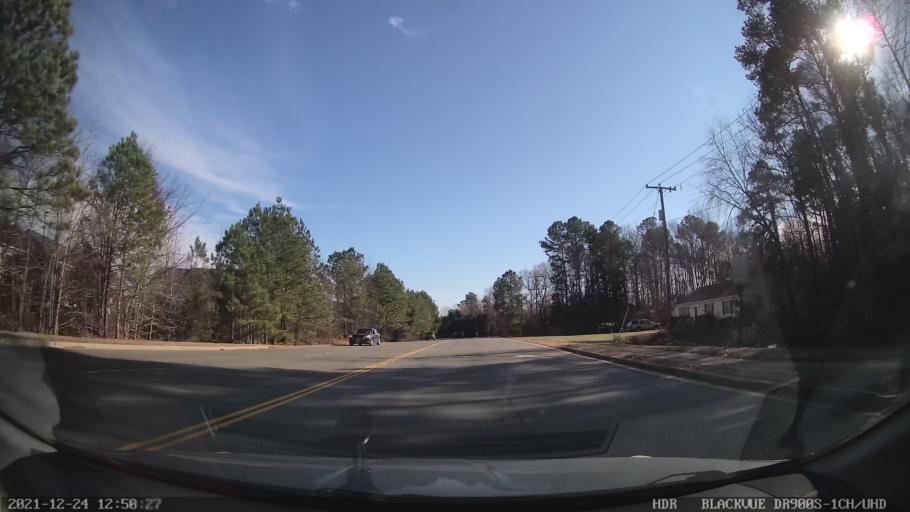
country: US
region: Virginia
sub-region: Henrico County
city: Short Pump
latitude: 37.6451
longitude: -77.6020
